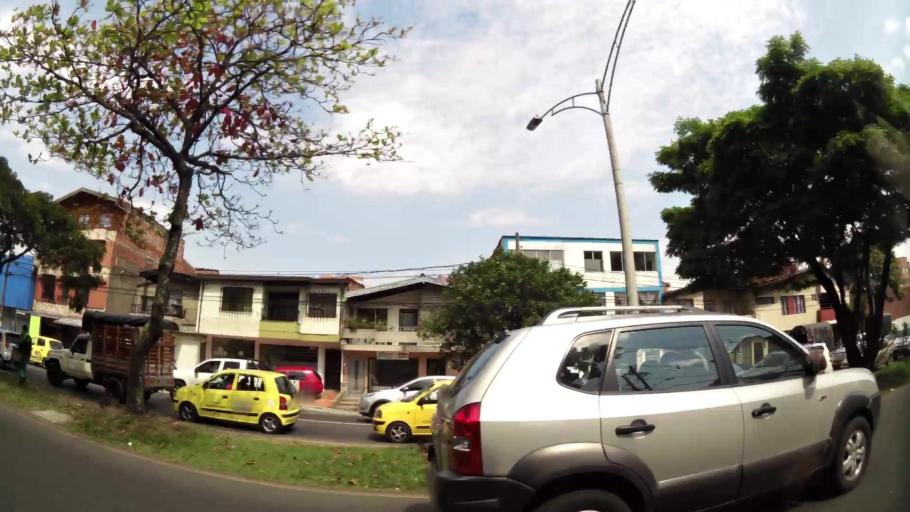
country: CO
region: Antioquia
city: Medellin
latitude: 6.2460
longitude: -75.5831
